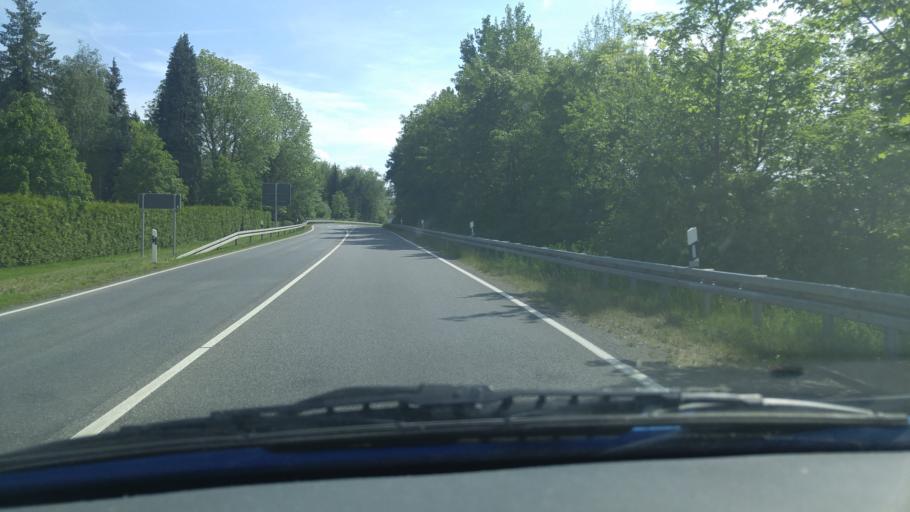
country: DE
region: Hesse
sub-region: Regierungsbezirk Giessen
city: Schotten
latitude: 50.5043
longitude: 9.1292
